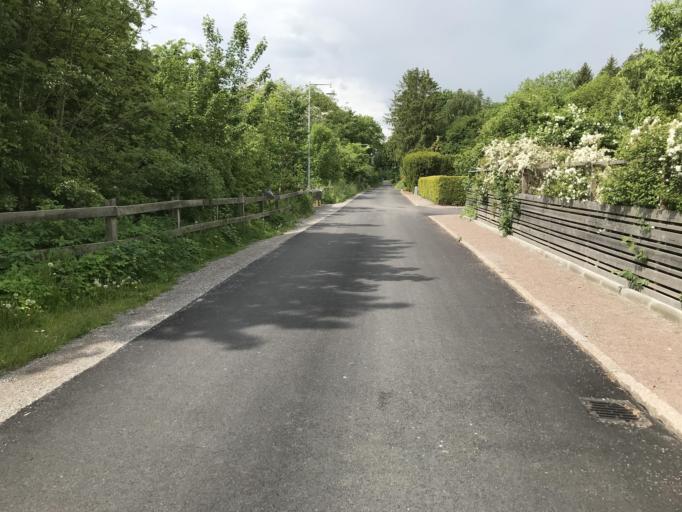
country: SE
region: Skane
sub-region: Landskrona
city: Landskrona
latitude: 55.9000
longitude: 12.8329
